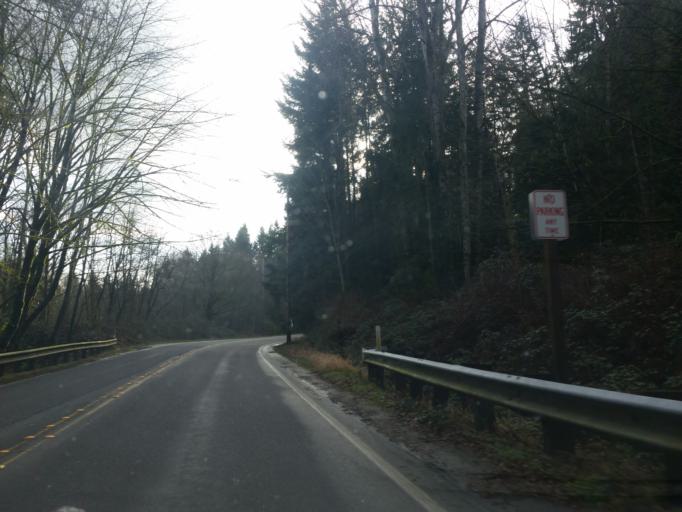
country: US
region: Washington
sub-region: King County
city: Kingsgate
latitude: 47.7314
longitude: -122.1566
